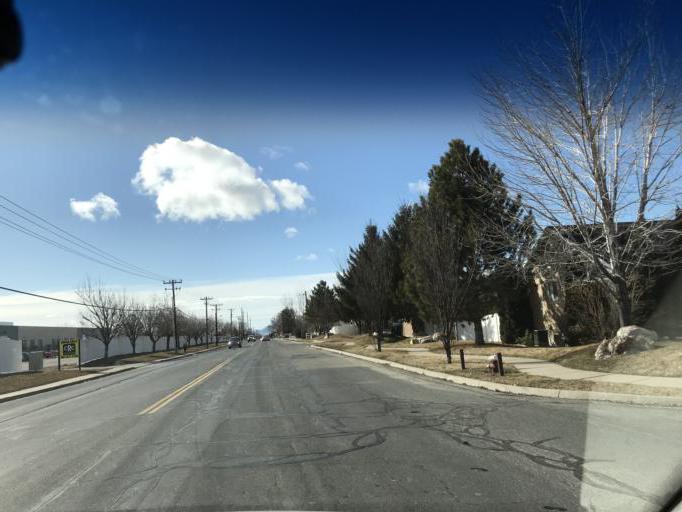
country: US
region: Utah
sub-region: Davis County
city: Woods Cross
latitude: 40.8747
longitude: -111.9070
